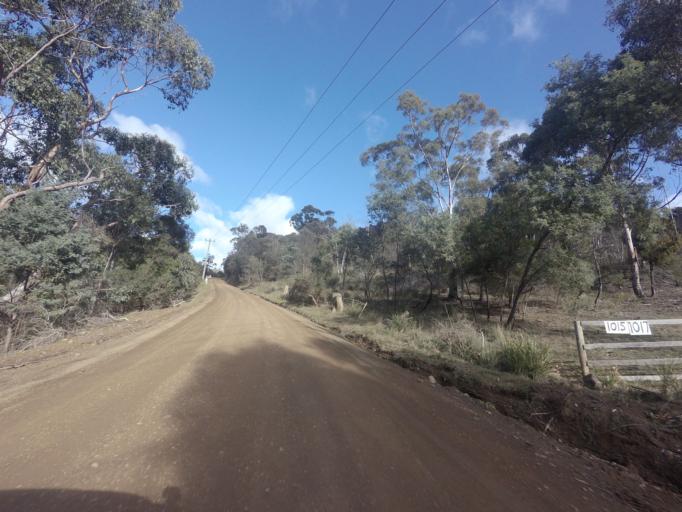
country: AU
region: Tasmania
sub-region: Derwent Valley
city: New Norfolk
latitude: -42.8169
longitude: 147.1279
